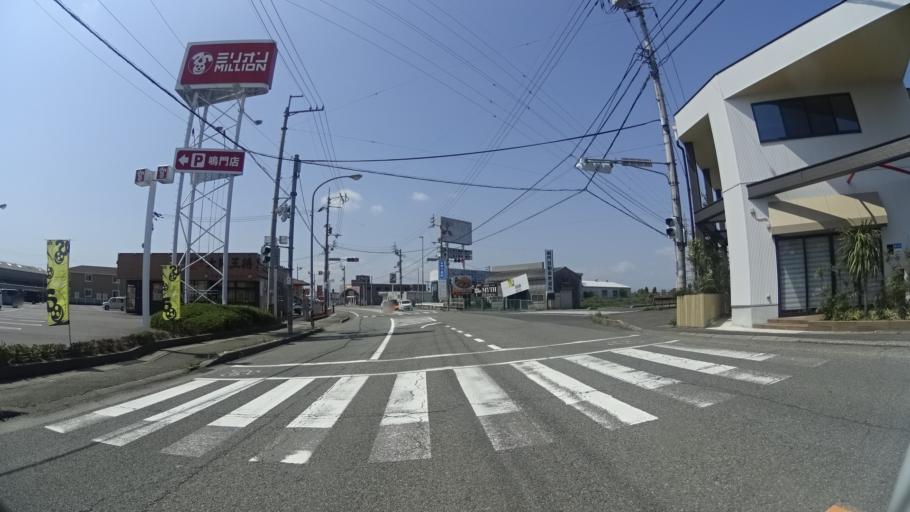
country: JP
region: Tokushima
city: Narutocho-mitsuishi
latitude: 34.1612
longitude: 134.5929
